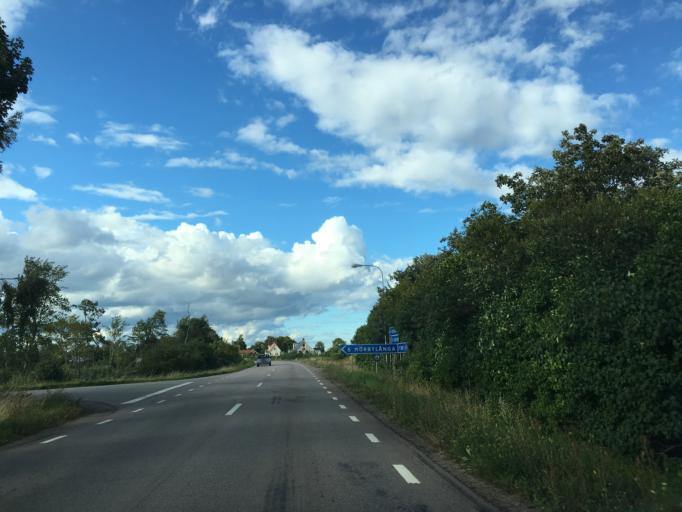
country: SE
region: Kalmar
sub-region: Morbylanga Kommun
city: Moerbylanga
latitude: 56.5149
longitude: 16.4389
